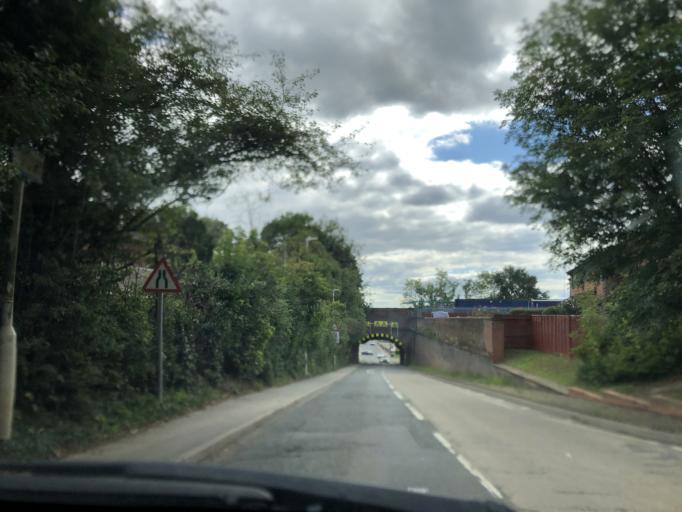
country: GB
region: England
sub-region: Kent
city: Edenbridge
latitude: 51.2092
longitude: 0.0608
